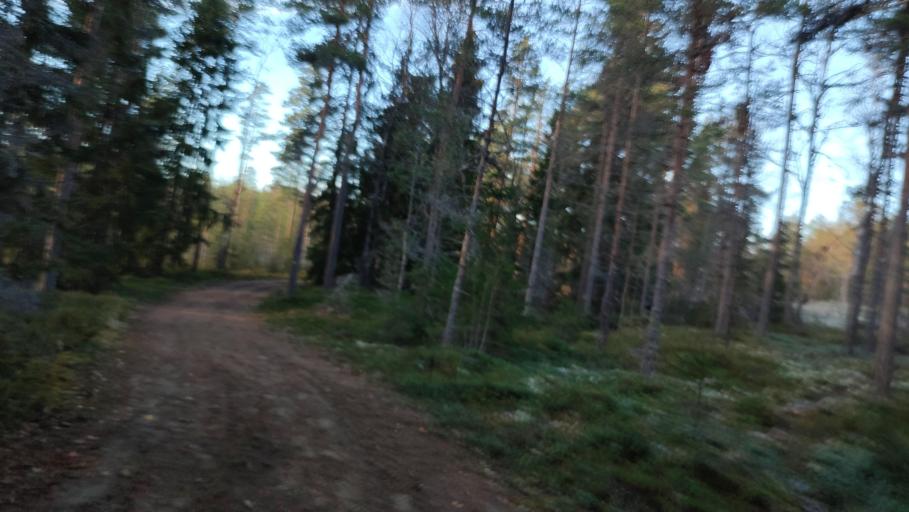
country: FI
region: Southern Ostrobothnia
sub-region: Suupohja
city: Karijoki
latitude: 62.2809
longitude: 21.6439
